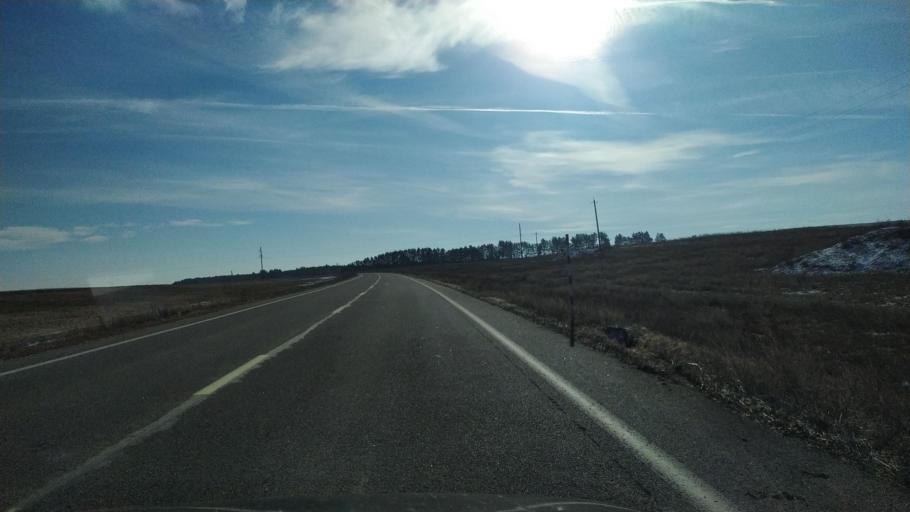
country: BY
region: Brest
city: Kamyanyets
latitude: 52.4080
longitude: 23.8572
